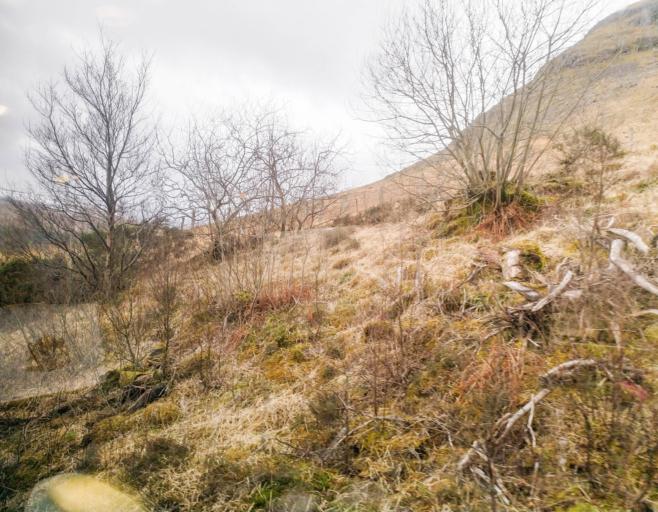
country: GB
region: Scotland
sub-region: Argyll and Bute
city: Garelochhead
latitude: 56.4887
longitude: -4.7111
